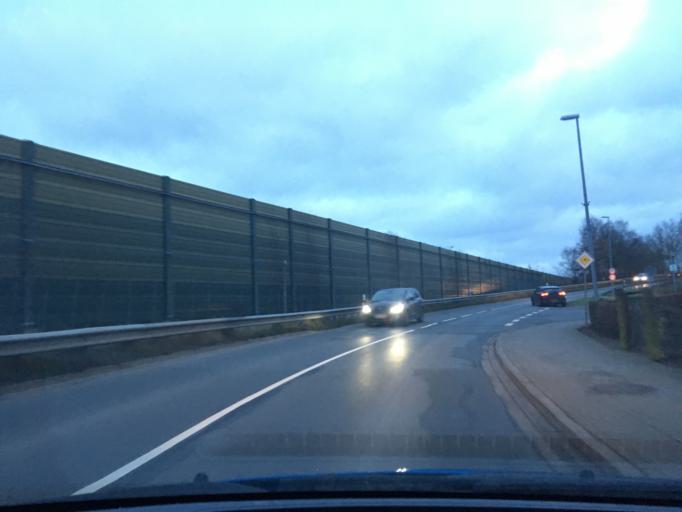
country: DE
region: Lower Saxony
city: Bardowick
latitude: 53.2899
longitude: 10.3728
